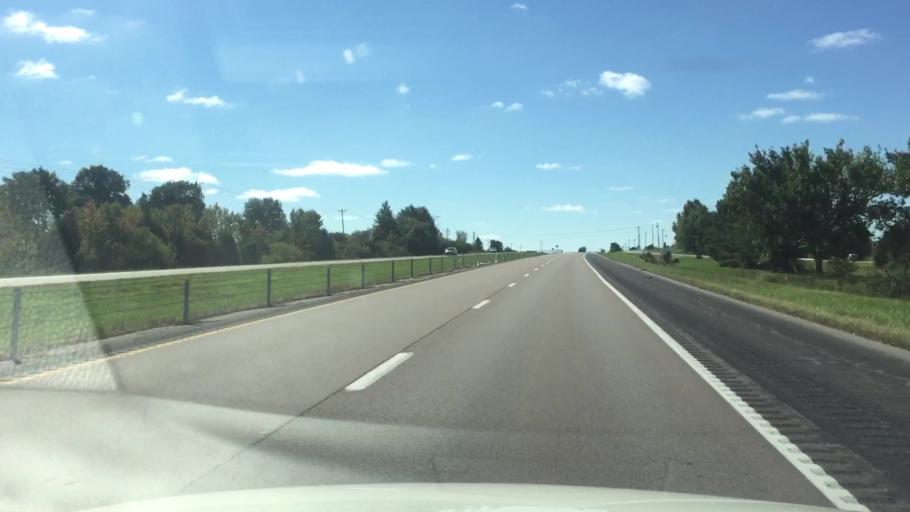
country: US
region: Missouri
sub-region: Boone County
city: Ashland
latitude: 38.8027
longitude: -92.2515
